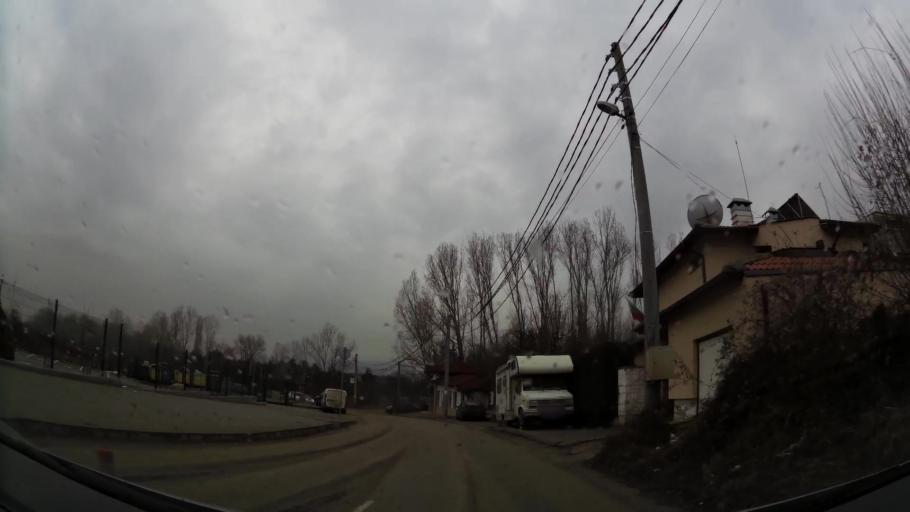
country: BG
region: Sofia-Capital
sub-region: Stolichna Obshtina
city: Sofia
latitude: 42.6208
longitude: 23.3787
